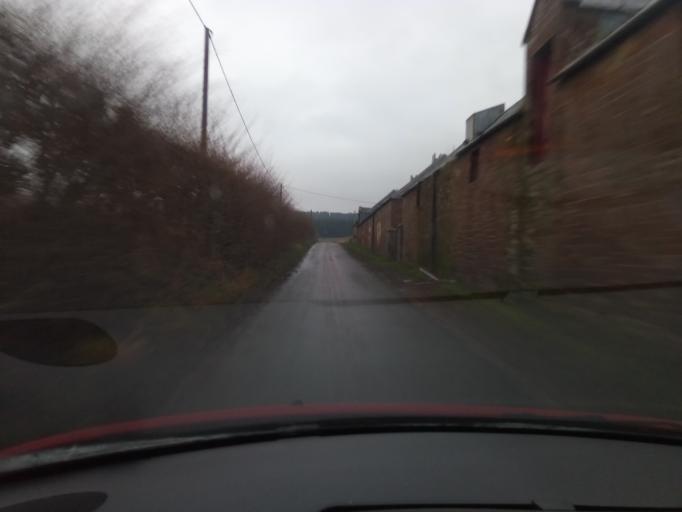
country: GB
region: Scotland
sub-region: The Scottish Borders
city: Kelso
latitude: 55.5395
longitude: -2.4424
